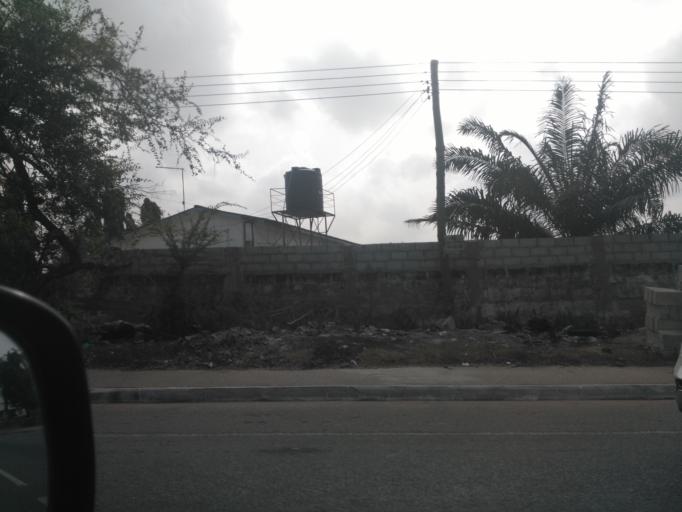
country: GH
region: Greater Accra
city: Accra
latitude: 5.5788
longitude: -0.1961
